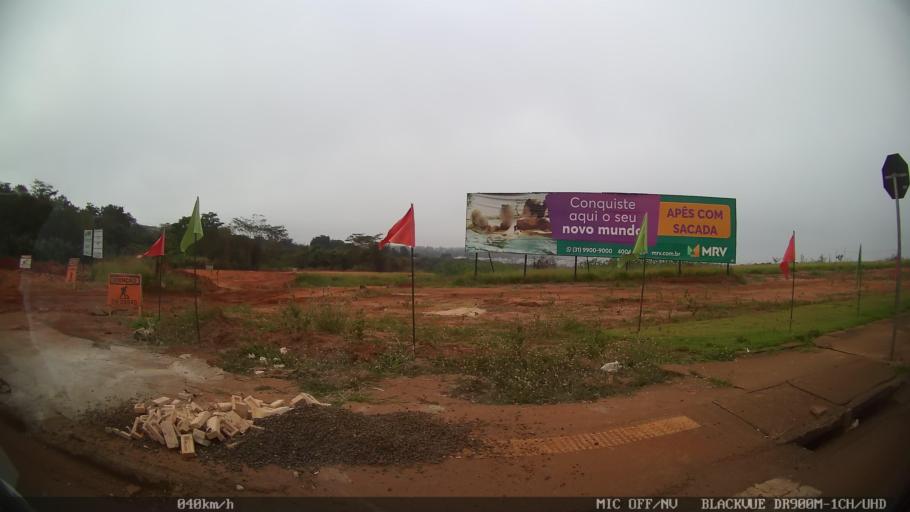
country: BR
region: Sao Paulo
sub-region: Sao Jose Do Rio Preto
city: Sao Jose do Rio Preto
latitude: -20.8503
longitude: -49.3701
